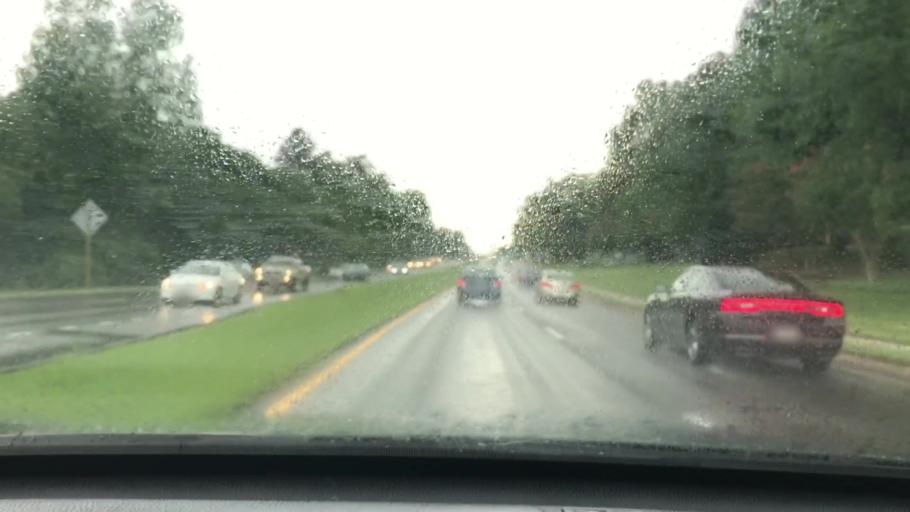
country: US
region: Virginia
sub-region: Henrico County
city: Laurel
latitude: 37.6298
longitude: -77.5234
